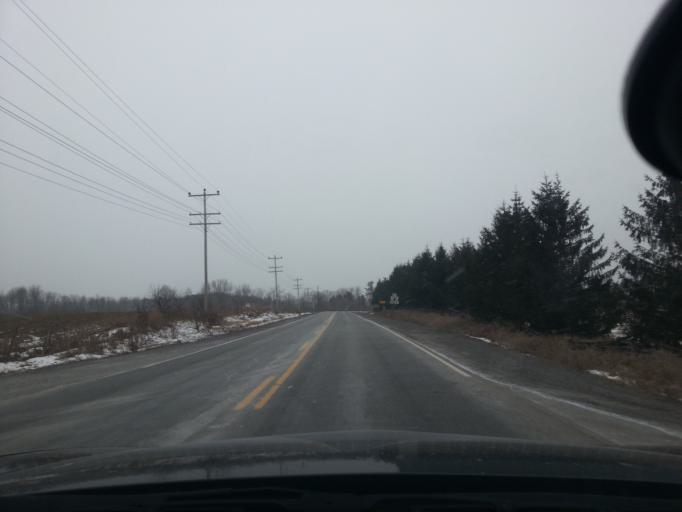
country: CA
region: Ontario
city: Arnprior
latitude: 45.3351
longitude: -76.2789
